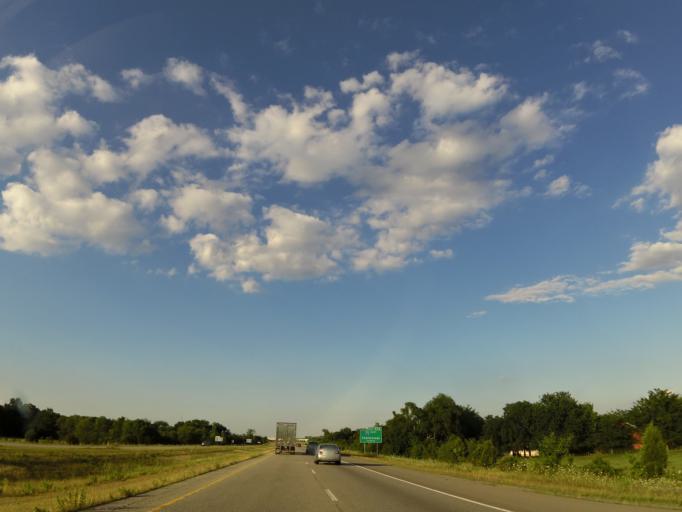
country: US
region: Tennessee
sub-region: Rutherford County
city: Murfreesboro
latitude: 35.8755
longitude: -86.4915
